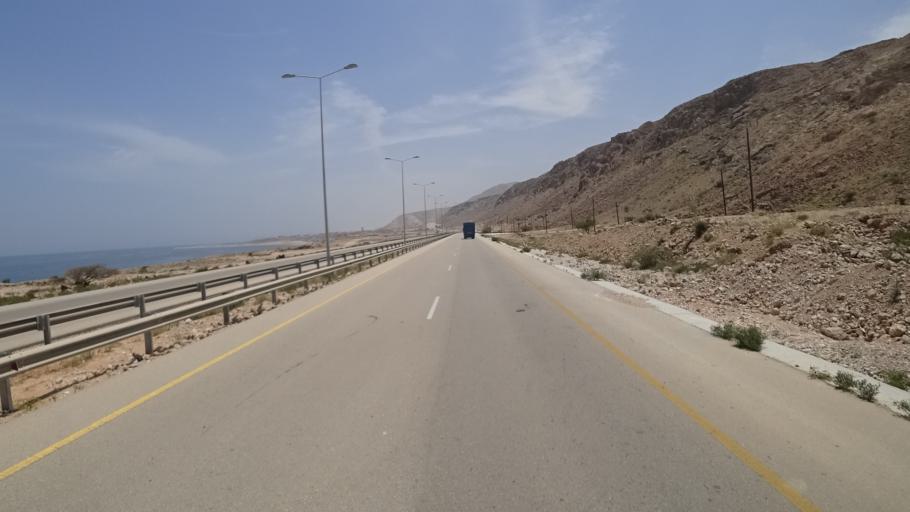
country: OM
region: Ash Sharqiyah
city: Sur
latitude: 22.7181
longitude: 59.3499
